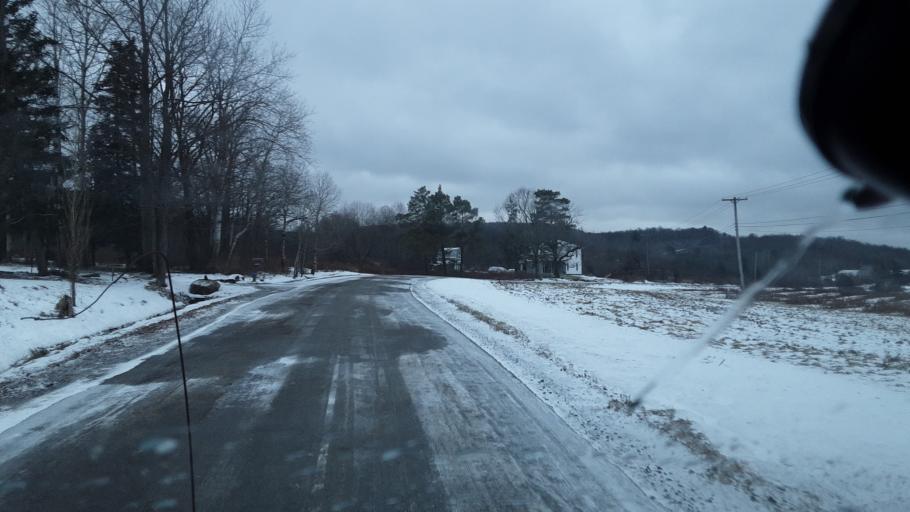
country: US
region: New York
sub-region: Allegany County
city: Friendship
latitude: 42.2943
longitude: -78.1539
